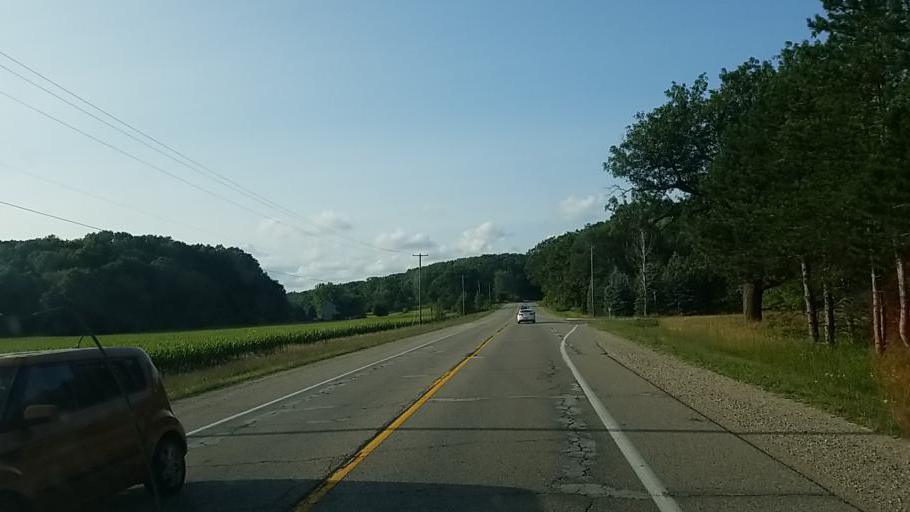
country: US
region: Michigan
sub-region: Kent County
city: Lowell
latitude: 42.9636
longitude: -85.3557
